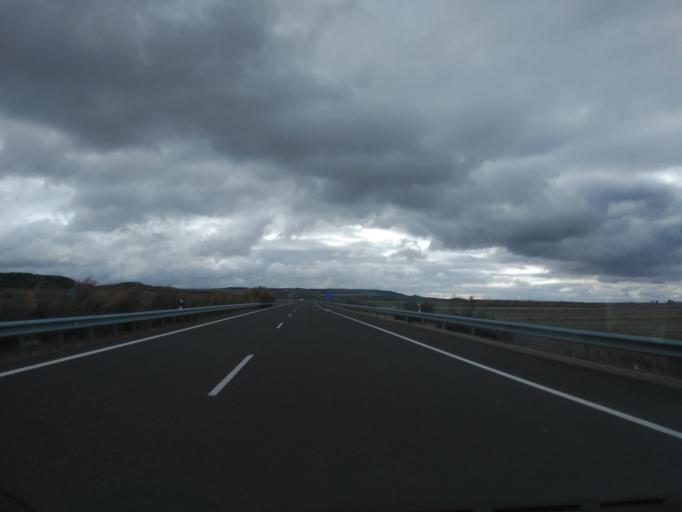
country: ES
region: Castille and Leon
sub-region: Provincia de Palencia
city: Amusco
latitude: 42.1841
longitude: -4.4500
